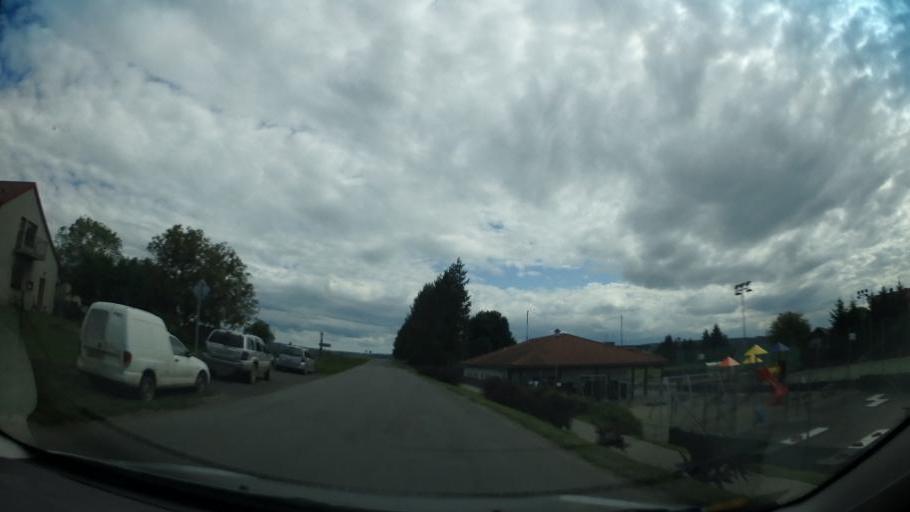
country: CZ
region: Pardubicky
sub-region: Okres Svitavy
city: Moravska Trebova
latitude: 49.7951
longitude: 16.6768
